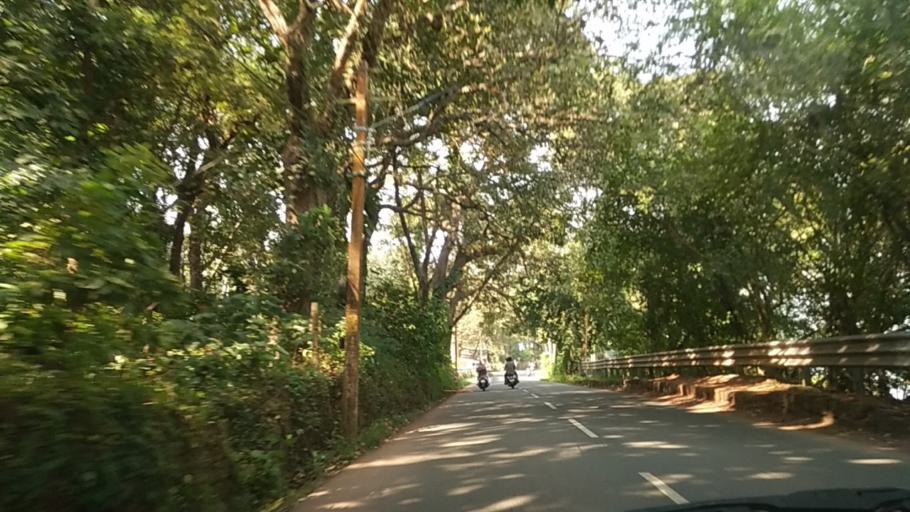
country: IN
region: Goa
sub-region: North Goa
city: Bambolim
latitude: 15.4998
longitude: 73.8843
